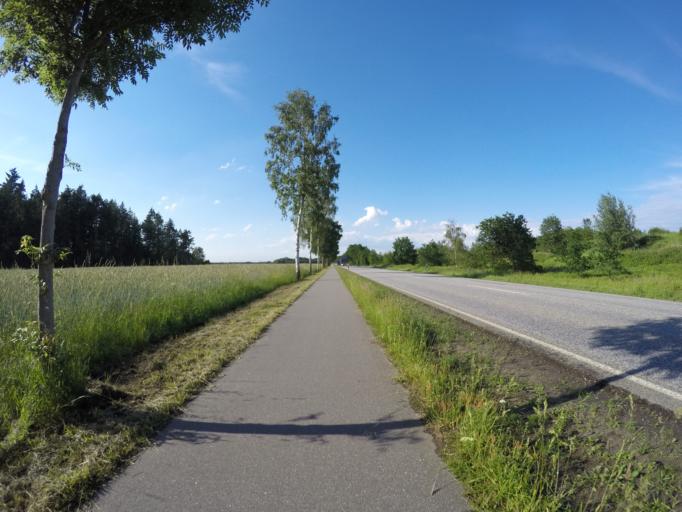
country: DE
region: Schleswig-Holstein
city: Lentfohrden
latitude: 53.8496
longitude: 9.8873
